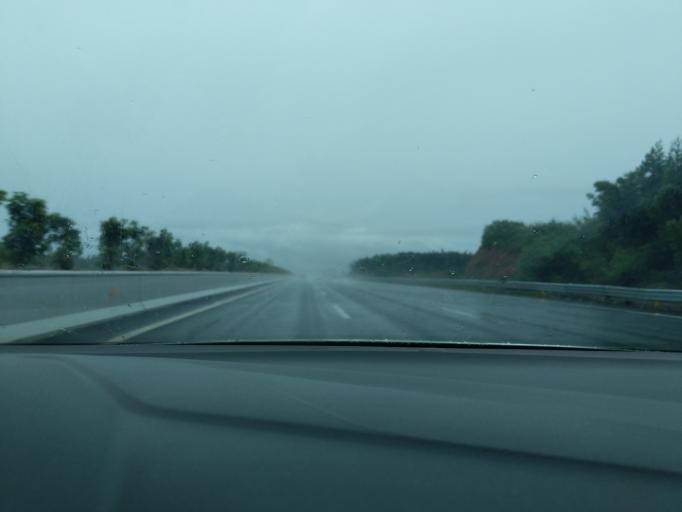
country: CN
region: Guangdong
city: Zhishan
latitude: 22.4853
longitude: 112.7883
